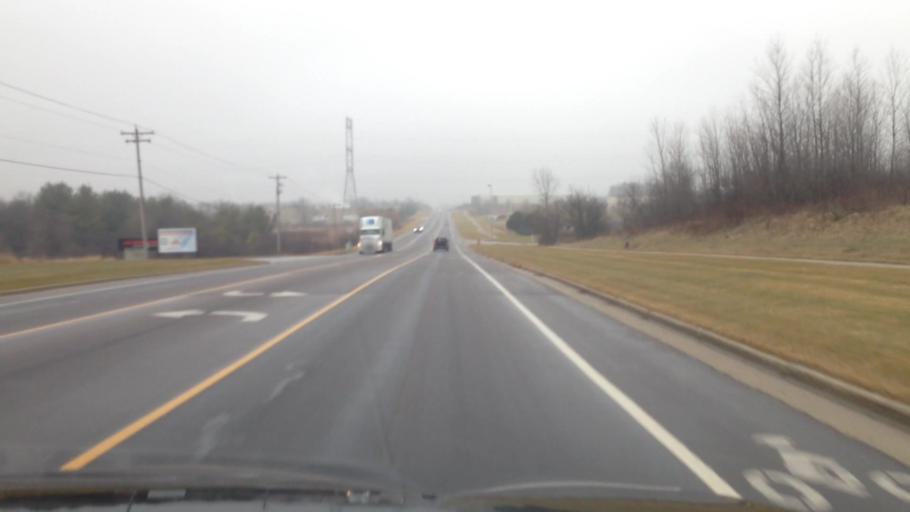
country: US
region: Wisconsin
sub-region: Washington County
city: Germantown
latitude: 43.2357
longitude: -88.1522
